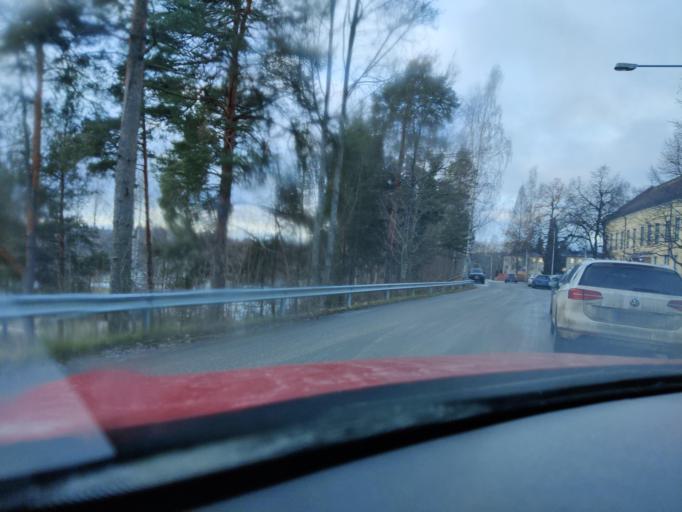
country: FI
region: Pirkanmaa
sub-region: Tampere
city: Nokia
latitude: 61.4767
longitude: 23.5067
